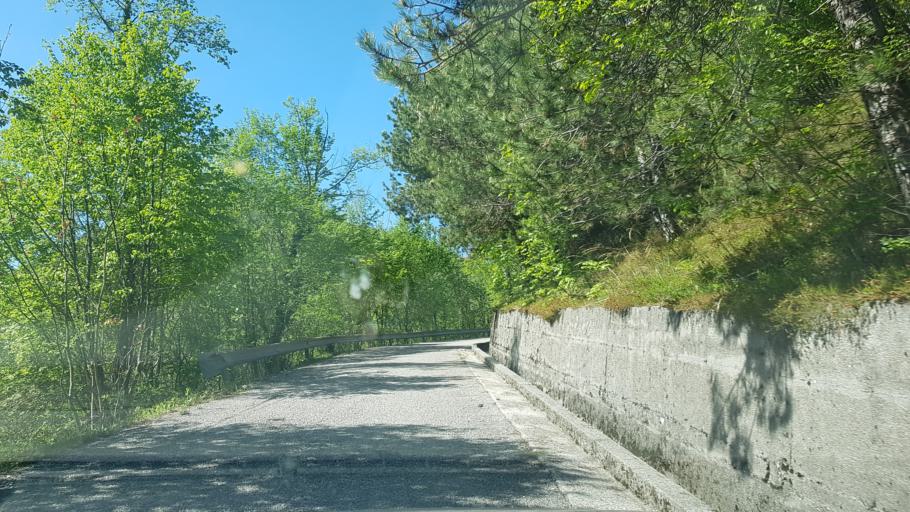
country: IT
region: Friuli Venezia Giulia
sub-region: Provincia di Udine
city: Trasaghis
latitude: 46.3141
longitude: 13.0440
